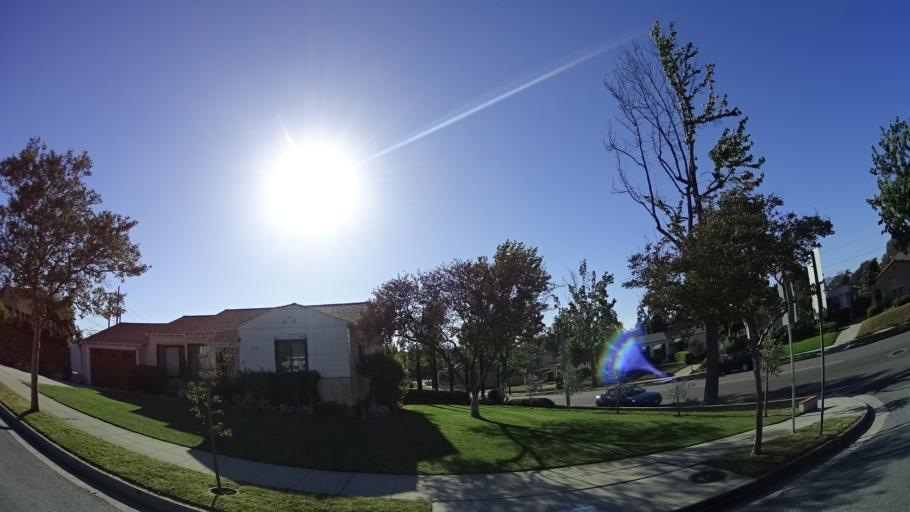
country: US
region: California
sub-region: Los Angeles County
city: Belvedere
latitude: 34.0695
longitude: -118.1586
